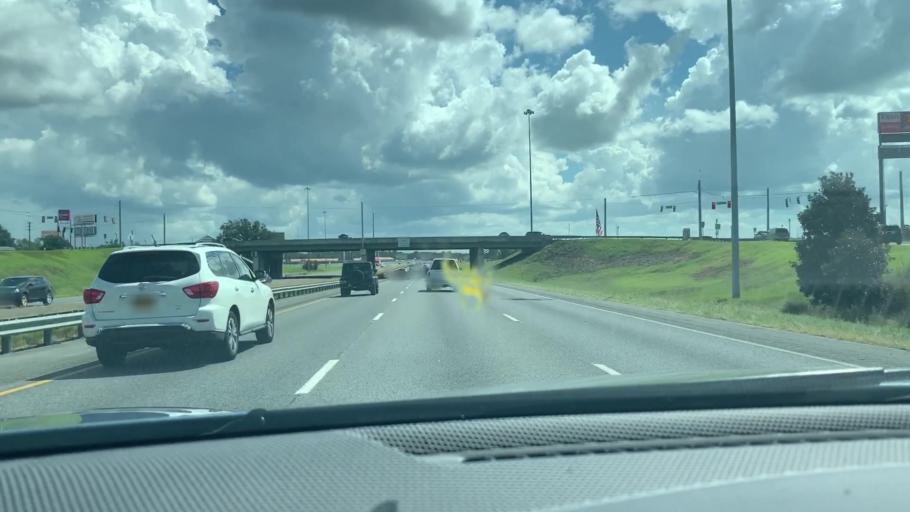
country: US
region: Georgia
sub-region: Lowndes County
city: Valdosta
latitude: 30.6810
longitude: -83.2242
